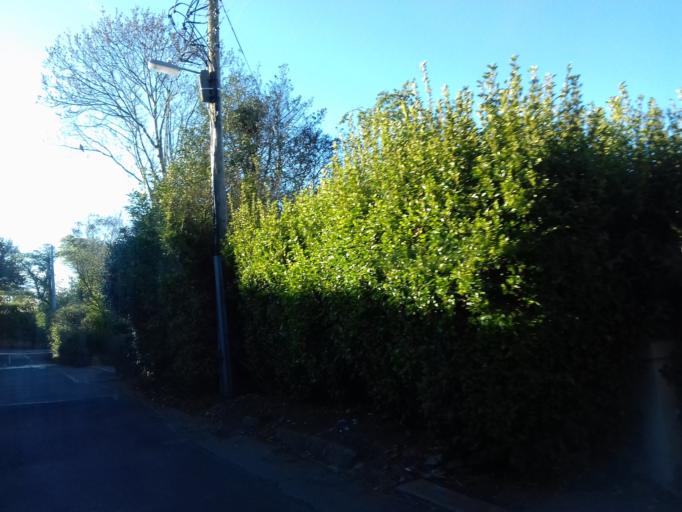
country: IE
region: Leinster
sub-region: Fingal County
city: Howth
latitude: 53.3767
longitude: -6.0633
